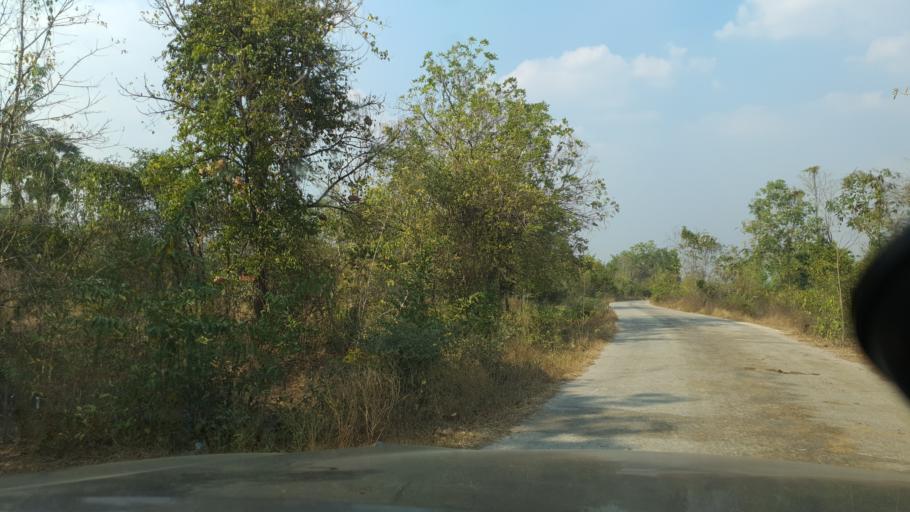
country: TH
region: Sukhothai
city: Ban Dan Lan Hoi
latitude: 17.0146
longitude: 99.5583
